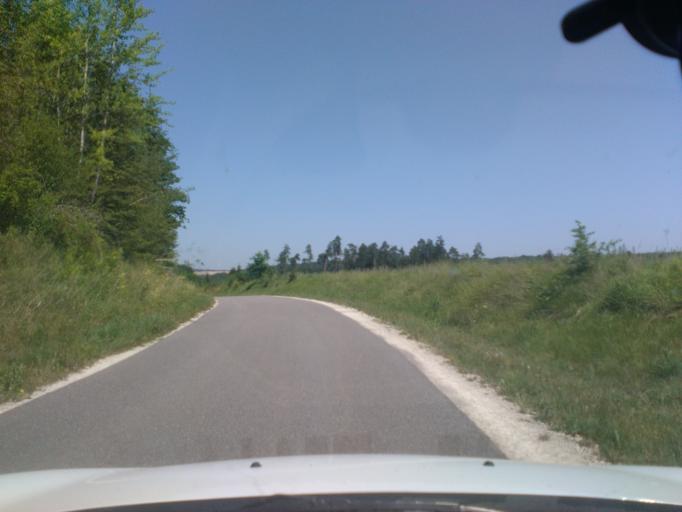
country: FR
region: Lorraine
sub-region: Departement des Vosges
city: Liffol-le-Grand
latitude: 48.4004
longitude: 5.5066
